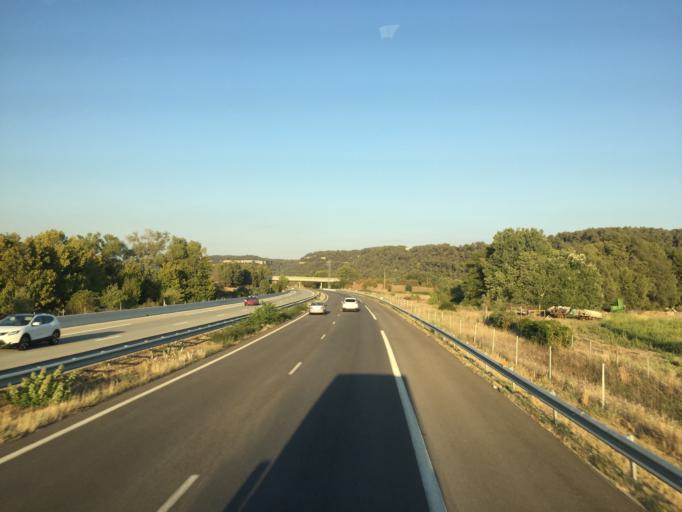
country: FR
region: Provence-Alpes-Cote d'Azur
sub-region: Departement des Bouches-du-Rhone
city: Peyrolles-en-Provence
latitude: 43.6558
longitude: 5.6050
